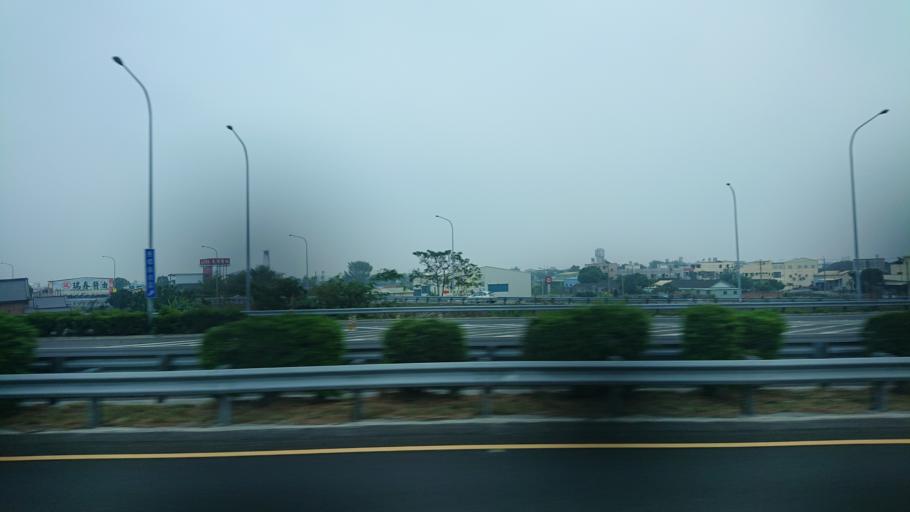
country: TW
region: Taiwan
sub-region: Yunlin
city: Douliu
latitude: 23.7780
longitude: 120.4736
